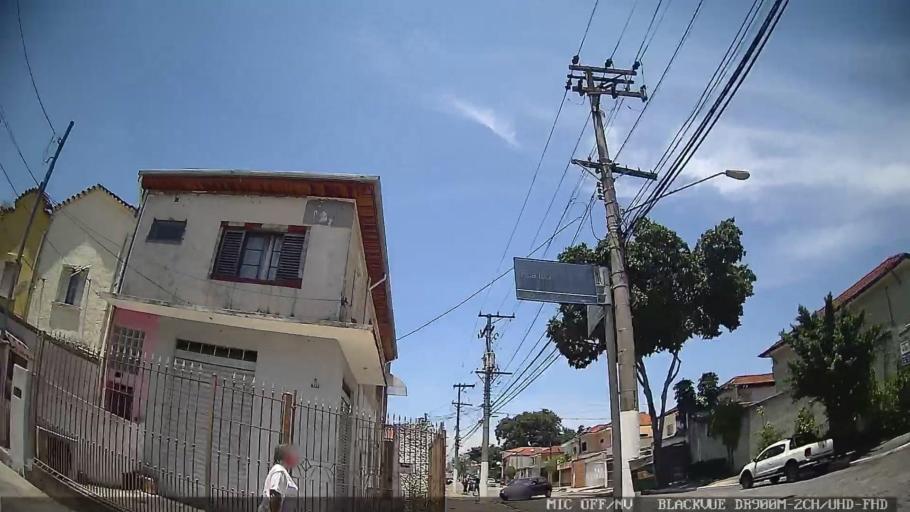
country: BR
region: Sao Paulo
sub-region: Sao Paulo
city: Sao Paulo
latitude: -23.5611
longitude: -46.5734
